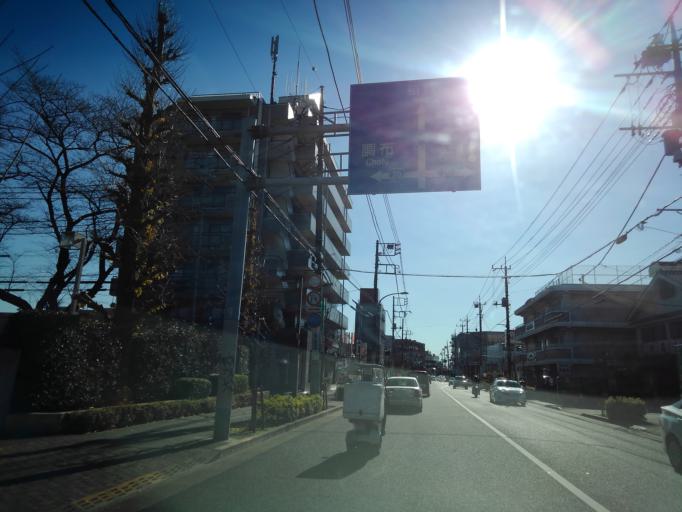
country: JP
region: Tokyo
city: Kokubunji
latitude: 35.6717
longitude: 139.4987
